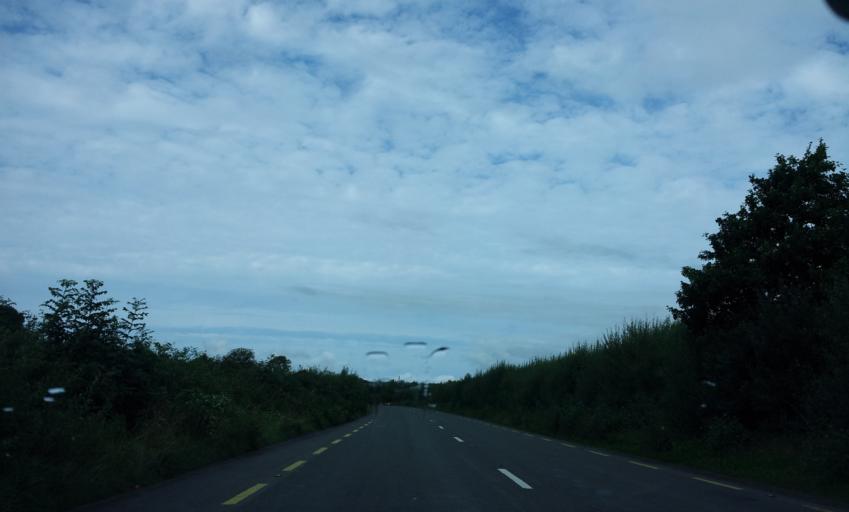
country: IE
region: Munster
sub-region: Ciarrai
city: Cill Airne
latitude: 52.0735
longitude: -9.6164
